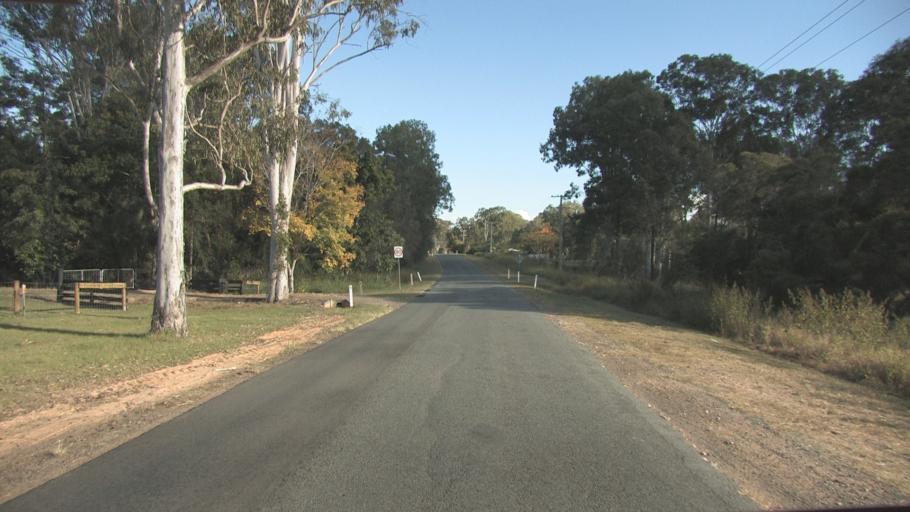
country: AU
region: Queensland
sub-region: Ipswich
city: Springfield Lakes
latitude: -27.7379
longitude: 152.9436
